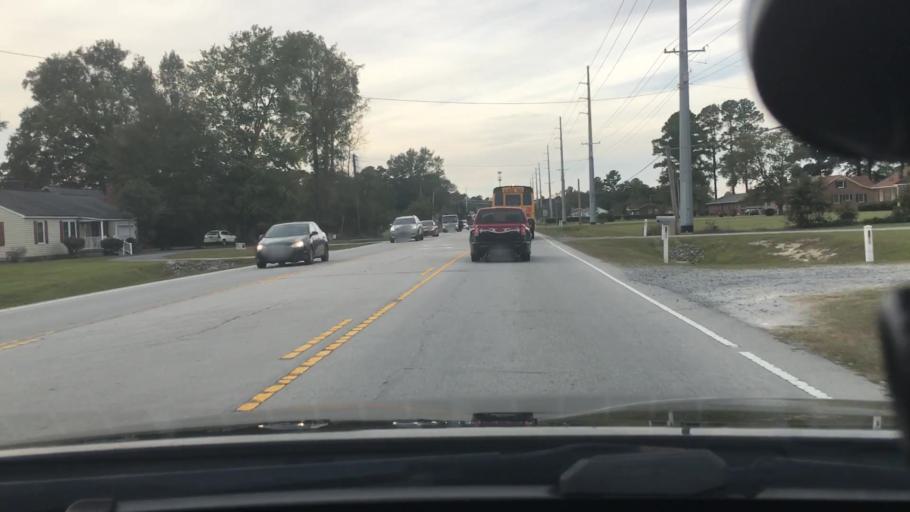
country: US
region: North Carolina
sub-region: Pitt County
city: Windsor
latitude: 35.5608
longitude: -77.3418
